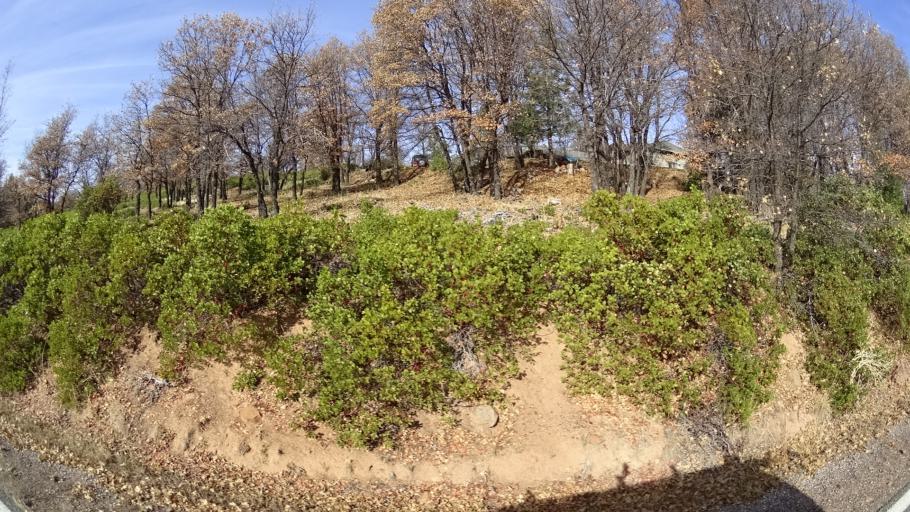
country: US
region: California
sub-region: Siskiyou County
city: Weed
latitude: 41.4039
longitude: -122.4108
